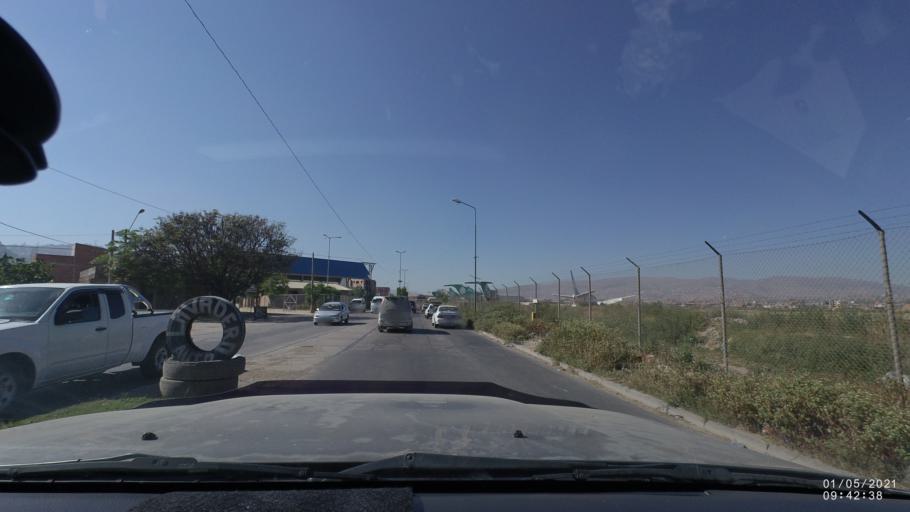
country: BO
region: Cochabamba
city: Cochabamba
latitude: -17.4278
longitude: -66.1654
